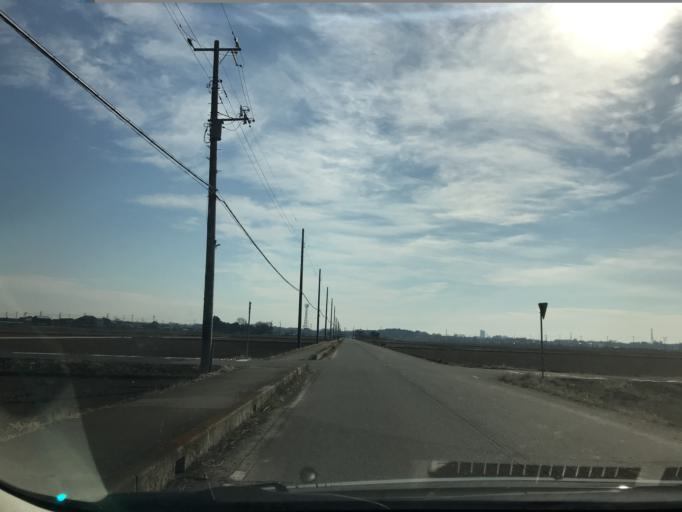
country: JP
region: Ibaraki
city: Mitsukaido
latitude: 36.0402
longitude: 140.0104
